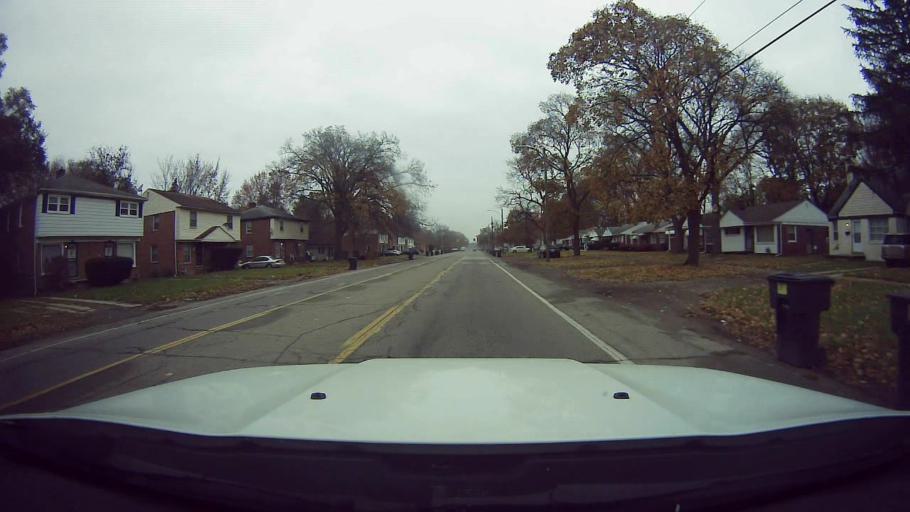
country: US
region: Michigan
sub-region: Oakland County
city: Southfield
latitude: 42.4347
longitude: -83.2584
